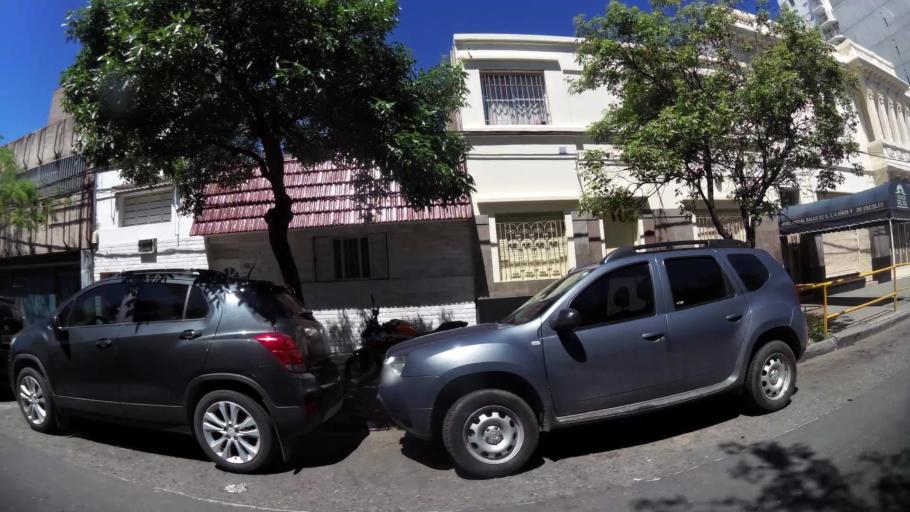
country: AR
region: Santa Fe
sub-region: Departamento de Rosario
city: Rosario
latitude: -32.9446
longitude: -60.6662
